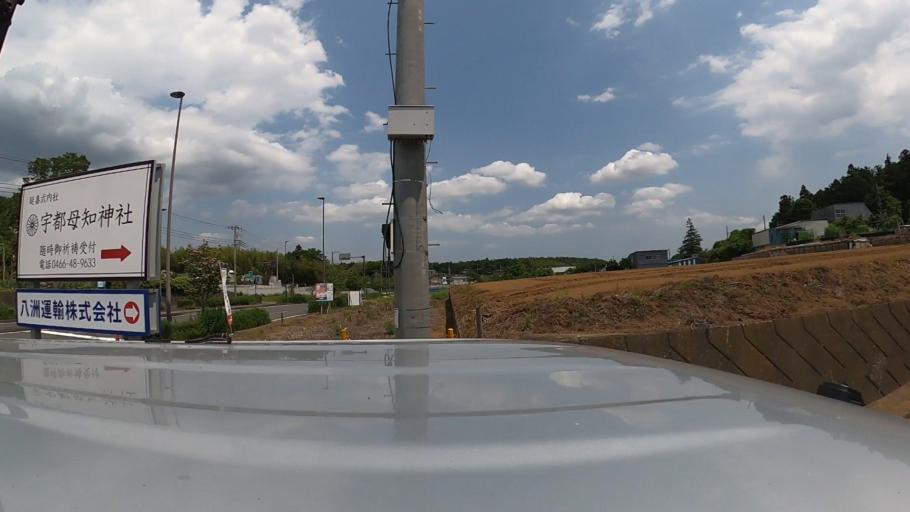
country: JP
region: Kanagawa
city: Chigasaki
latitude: 35.3935
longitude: 139.4208
